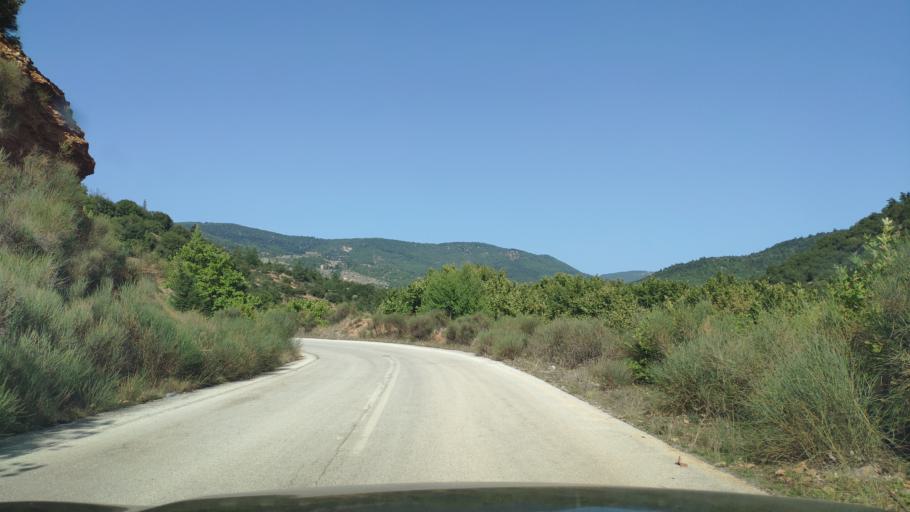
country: GR
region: West Greece
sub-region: Nomos Achaias
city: Aiyira
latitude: 37.9802
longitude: 22.3536
